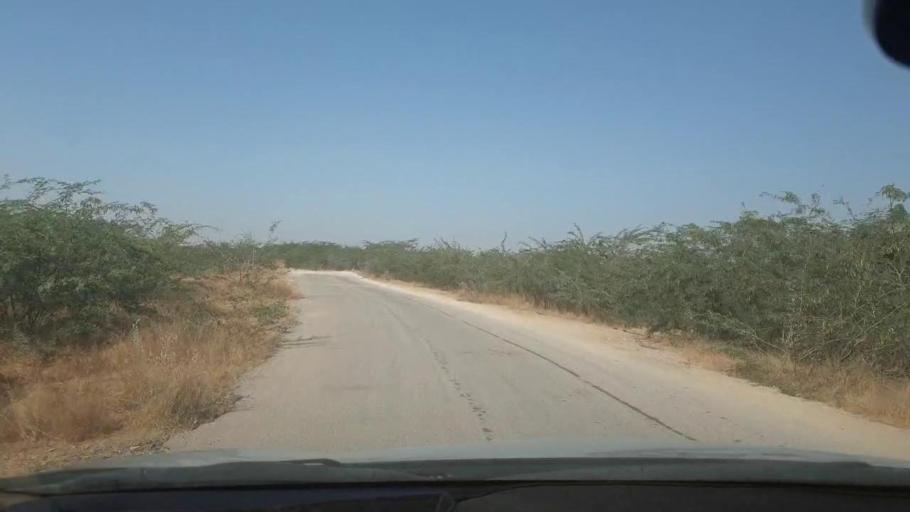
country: PK
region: Sindh
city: Malir Cantonment
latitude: 25.1464
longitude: 67.1665
